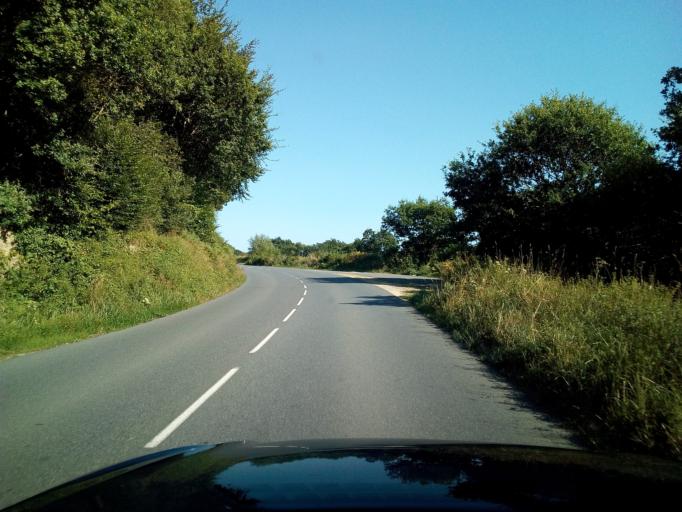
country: FR
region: Brittany
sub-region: Departement du Finistere
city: Landivisiau
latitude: 48.4968
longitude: -4.0874
